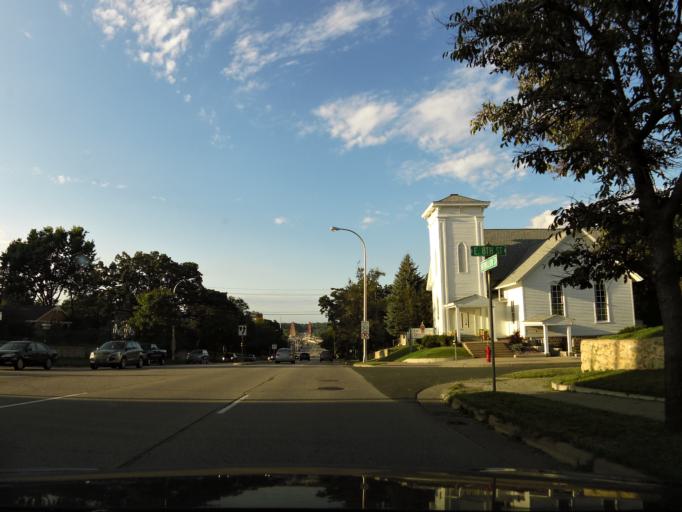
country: US
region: Minnesota
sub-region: Dakota County
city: Hastings
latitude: 44.7379
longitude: -92.8525
